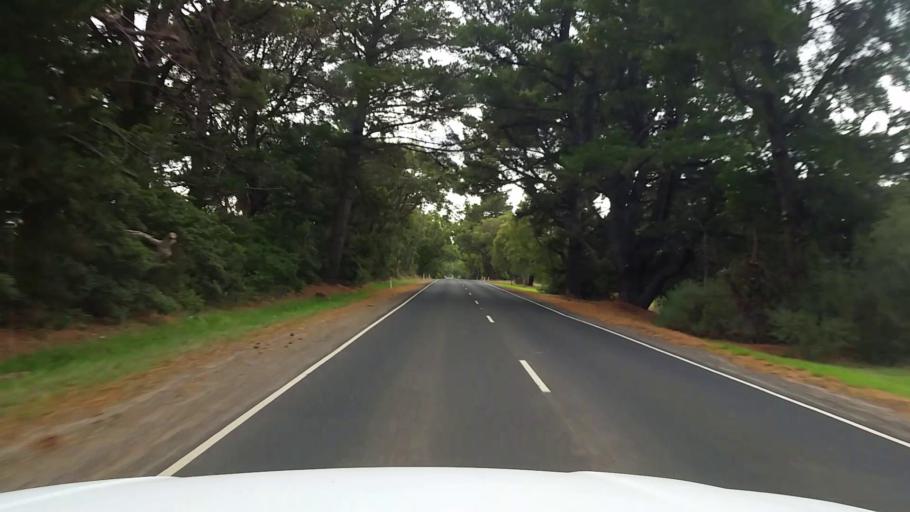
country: AU
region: Victoria
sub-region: Mornington Peninsula
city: Merricks
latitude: -38.4102
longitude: 145.0604
